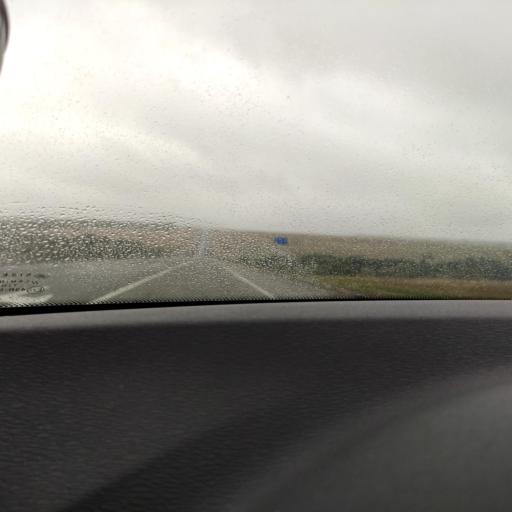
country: RU
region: Samara
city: Yelkhovka
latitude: 53.7406
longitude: 50.2276
